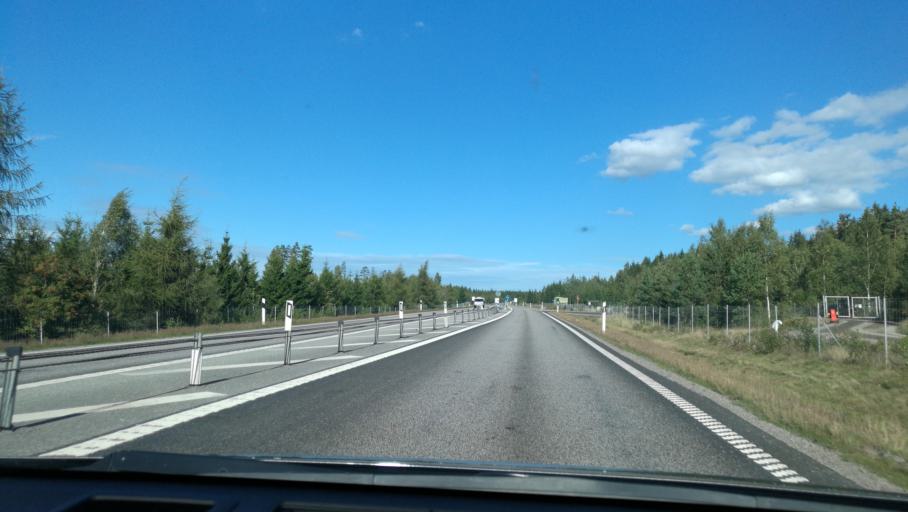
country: SE
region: Vaestra Goetaland
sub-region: Toreboda Kommun
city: Toereboda
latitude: 58.7909
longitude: 14.0192
